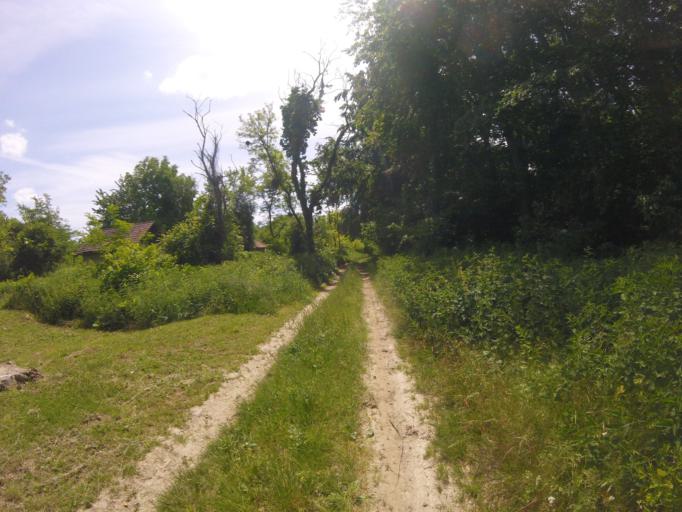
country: HU
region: Zala
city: Zalaszentgrot
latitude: 46.8932
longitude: 17.0330
